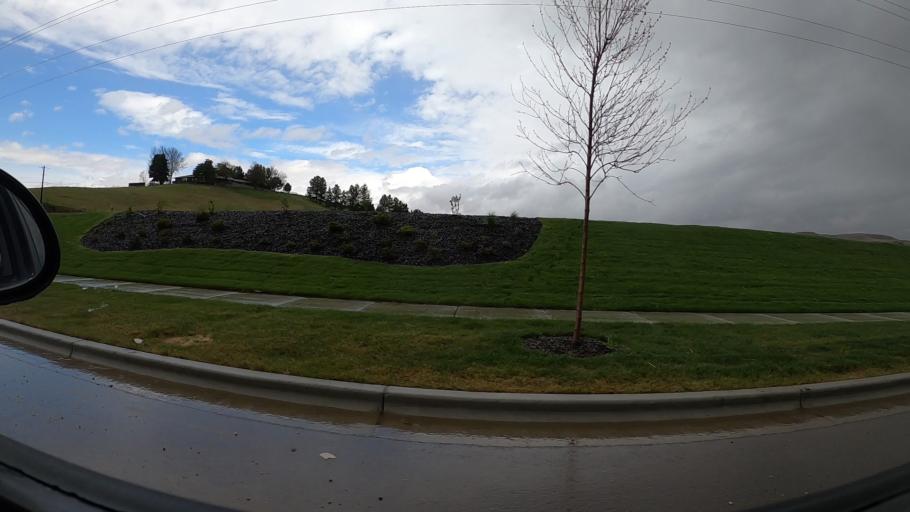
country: US
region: Idaho
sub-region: Ada County
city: Eagle
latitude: 43.7358
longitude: -116.2893
